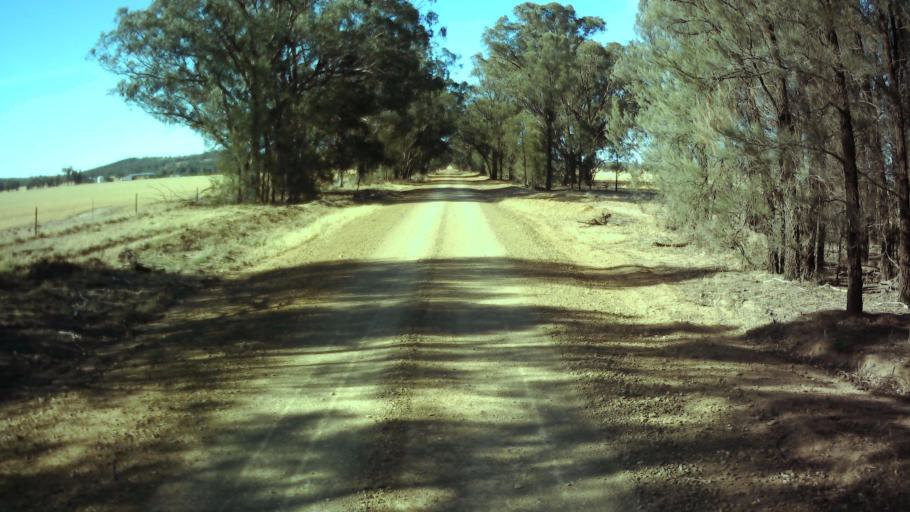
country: AU
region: New South Wales
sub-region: Weddin
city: Grenfell
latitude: -33.8177
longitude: 147.8760
